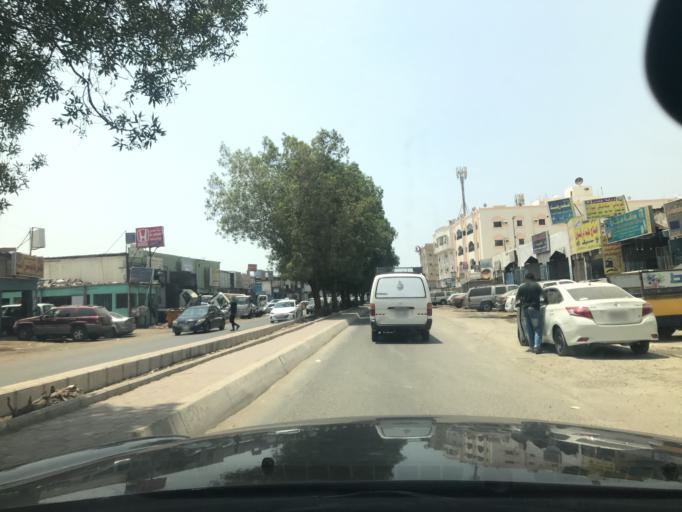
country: SA
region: Makkah
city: Jeddah
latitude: 21.4603
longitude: 39.2283
